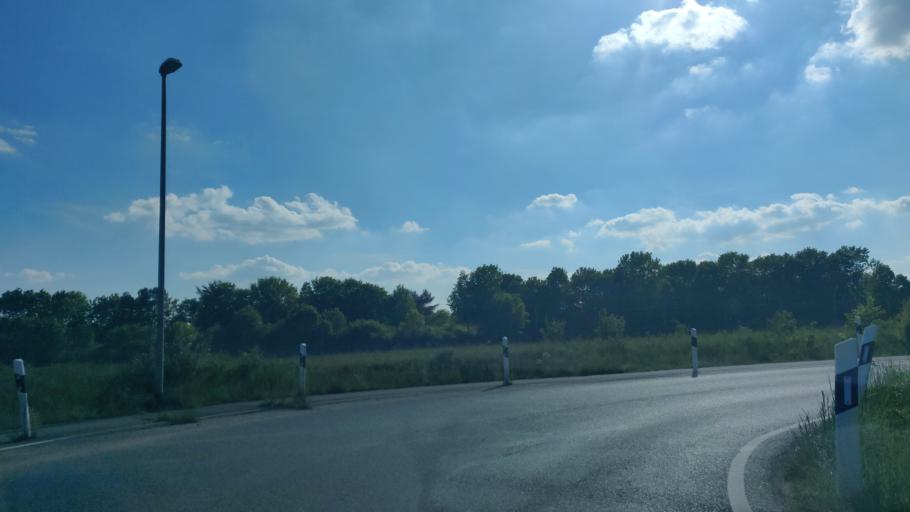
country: DE
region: Lower Saxony
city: Isernhagen Farster Bauerschaft
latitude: 52.4157
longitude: 9.8341
